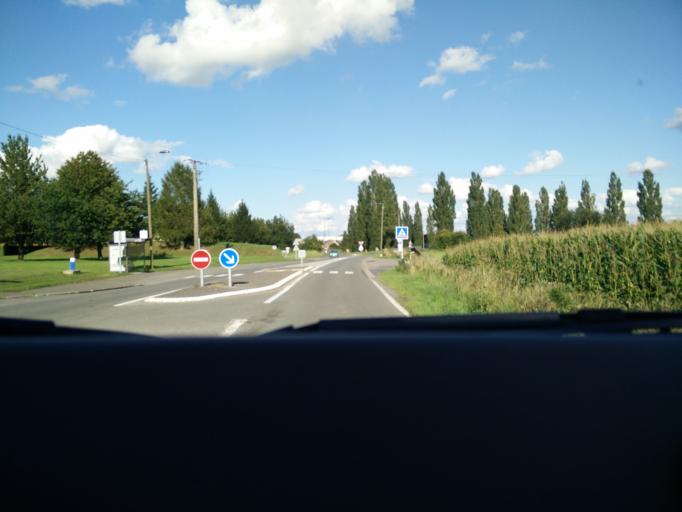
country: FR
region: Nord-Pas-de-Calais
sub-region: Departement du Nord
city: Rousies
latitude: 50.2860
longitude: 4.0024
